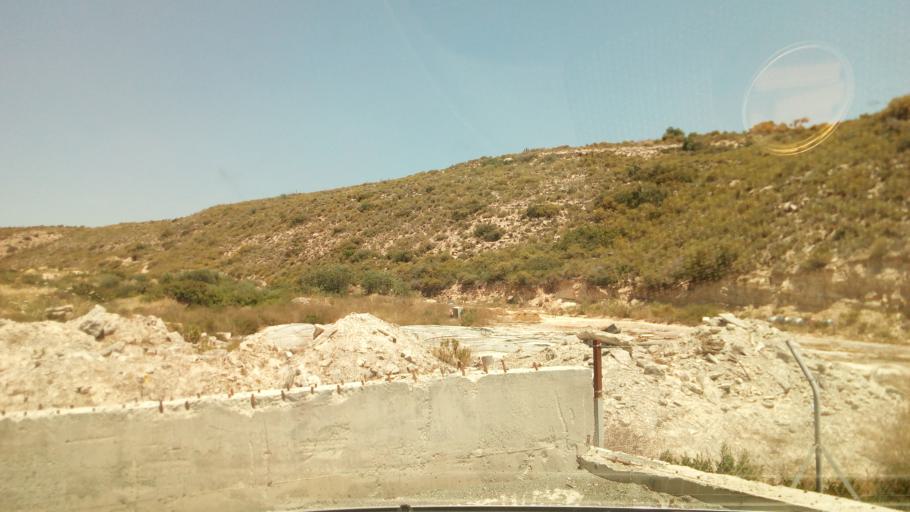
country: CY
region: Limassol
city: Ypsonas
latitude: 34.7322
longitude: 32.9566
